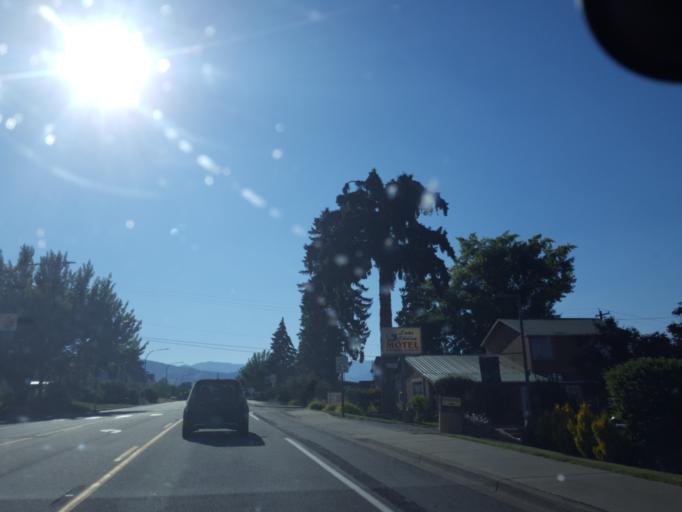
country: US
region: Washington
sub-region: Chelan County
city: Chelan
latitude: 47.8355
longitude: -120.0494
